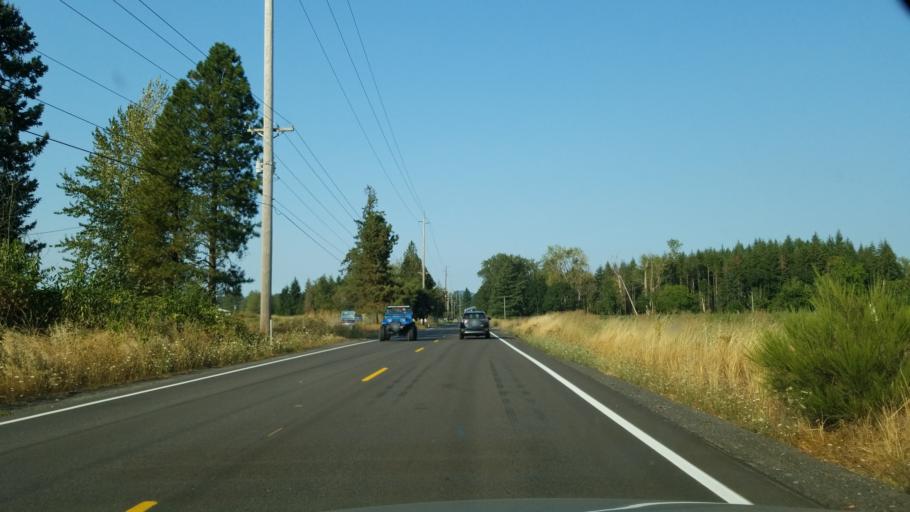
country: US
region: Oregon
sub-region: Clackamas County
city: Molalla
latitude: 45.1570
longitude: -122.5497
